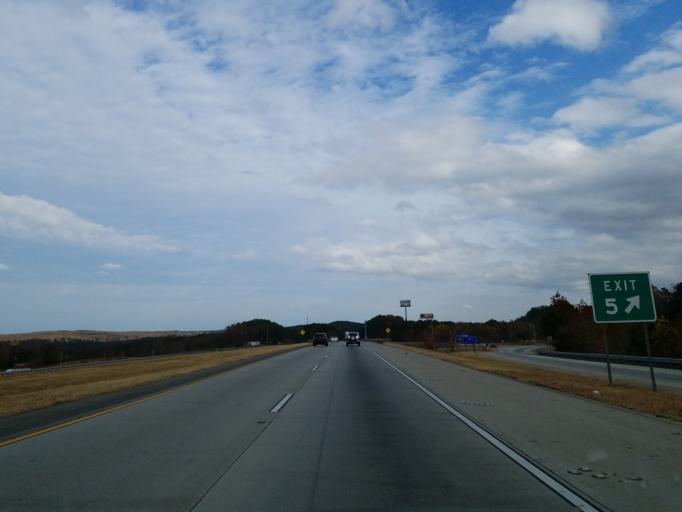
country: US
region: Georgia
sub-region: Haralson County
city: Tallapoosa
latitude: 33.6836
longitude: -85.2656
